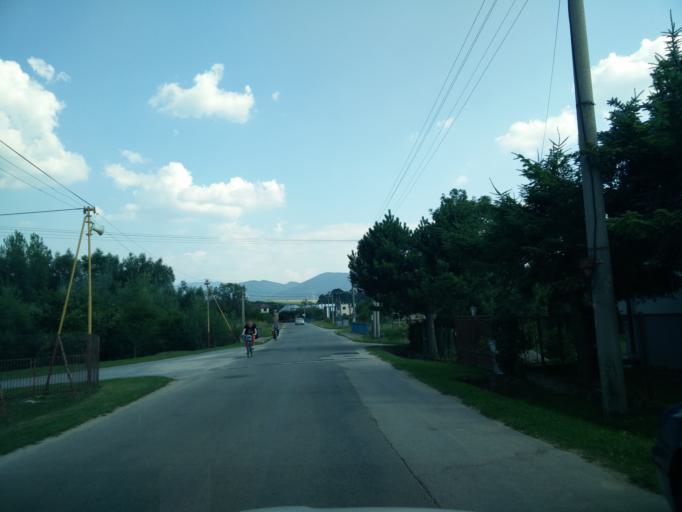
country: SK
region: Zilinsky
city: Rajec
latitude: 49.1089
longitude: 18.6400
